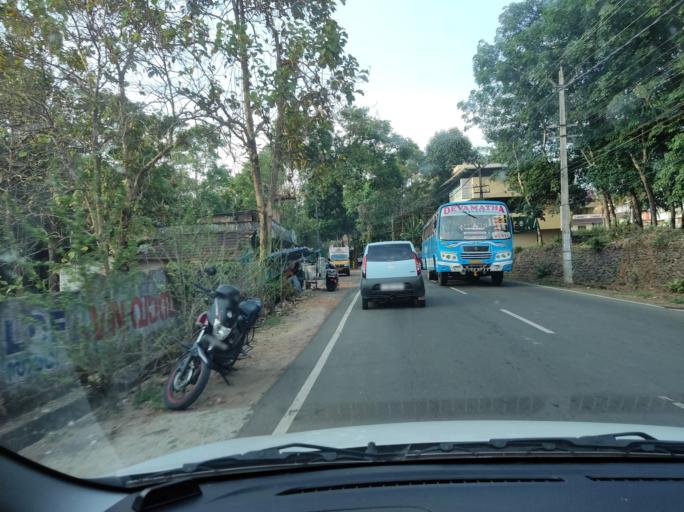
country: IN
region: Kerala
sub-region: Kottayam
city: Kottayam
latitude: 9.6431
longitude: 76.5340
